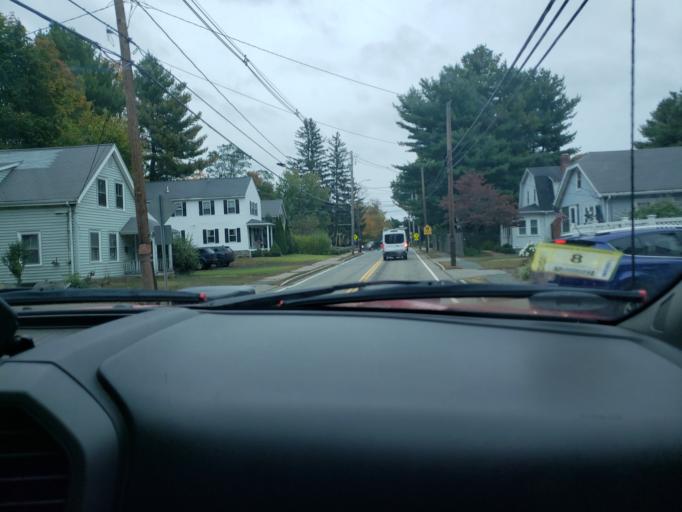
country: US
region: Massachusetts
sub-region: Middlesex County
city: Natick
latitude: 42.2764
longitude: -71.3510
